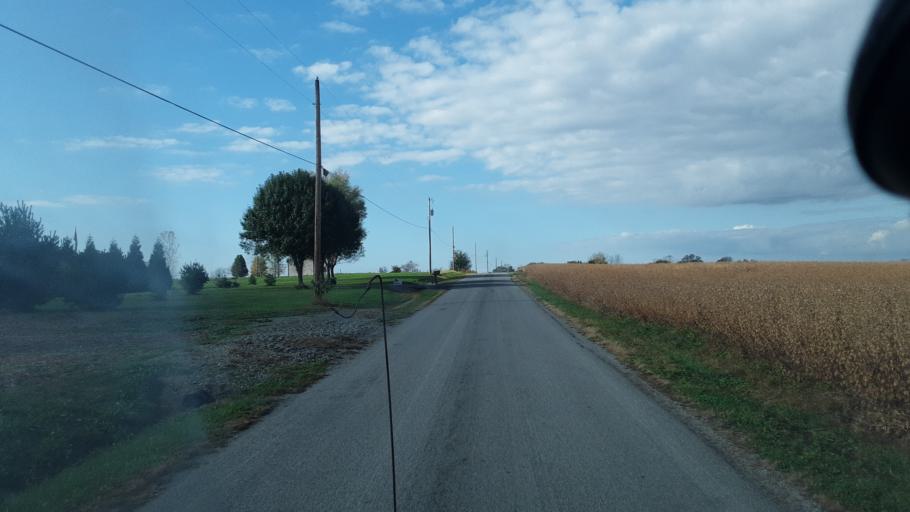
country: US
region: Ohio
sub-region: Highland County
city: Leesburg
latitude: 39.3251
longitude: -83.4841
